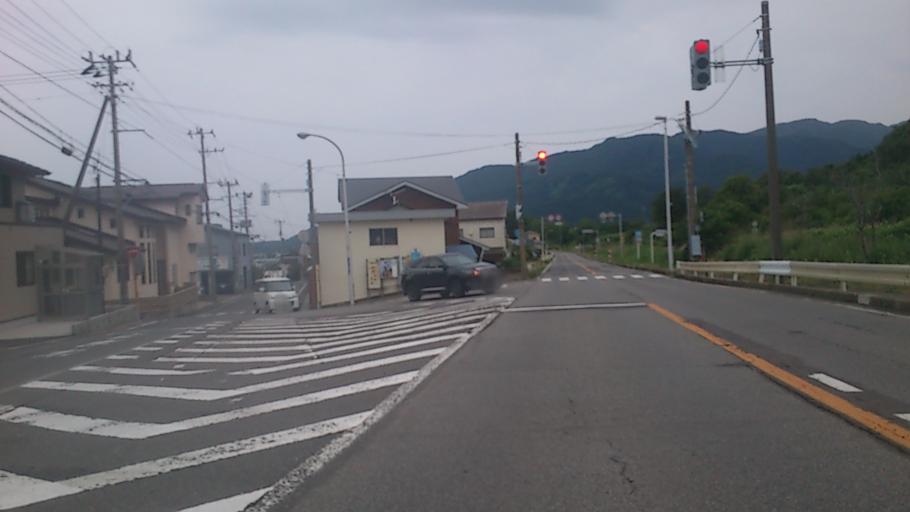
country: JP
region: Akita
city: Noshiromachi
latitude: 40.3613
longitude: 140.0233
